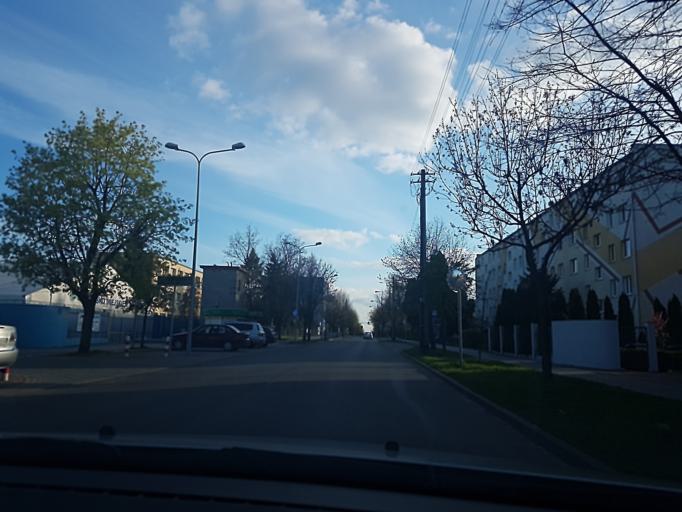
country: PL
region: Lodz Voivodeship
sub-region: Powiat kutnowski
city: Kutno
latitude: 52.2357
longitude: 19.3670
